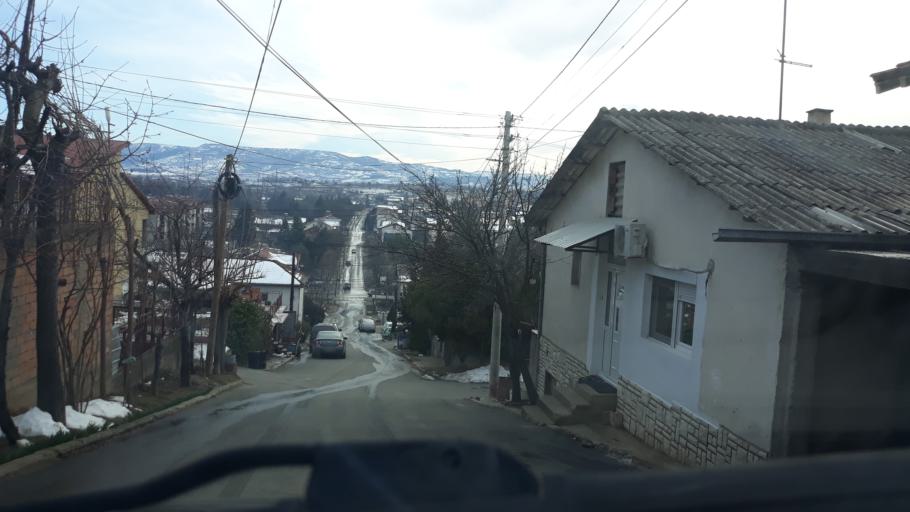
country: MK
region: Negotino
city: Negotino
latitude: 41.4842
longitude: 22.0825
